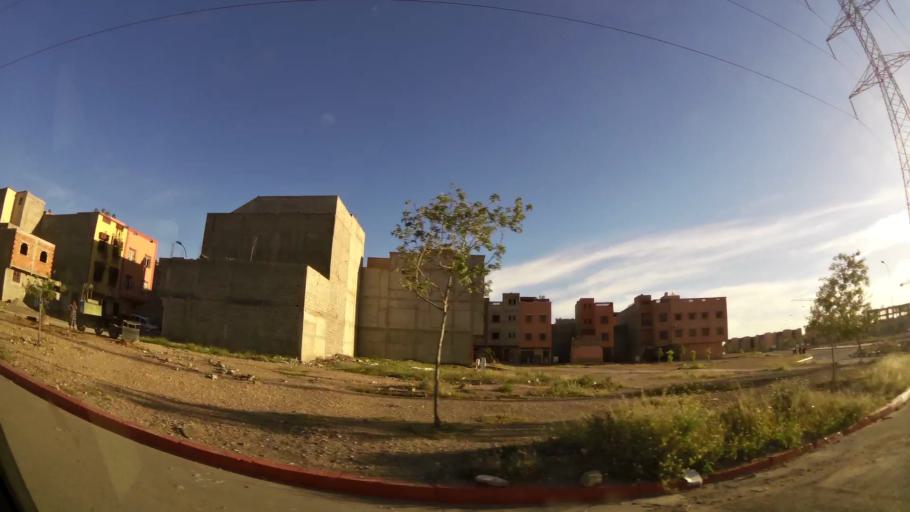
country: MA
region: Marrakech-Tensift-Al Haouz
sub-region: Marrakech
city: Marrakesh
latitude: 31.7430
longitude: -8.1224
